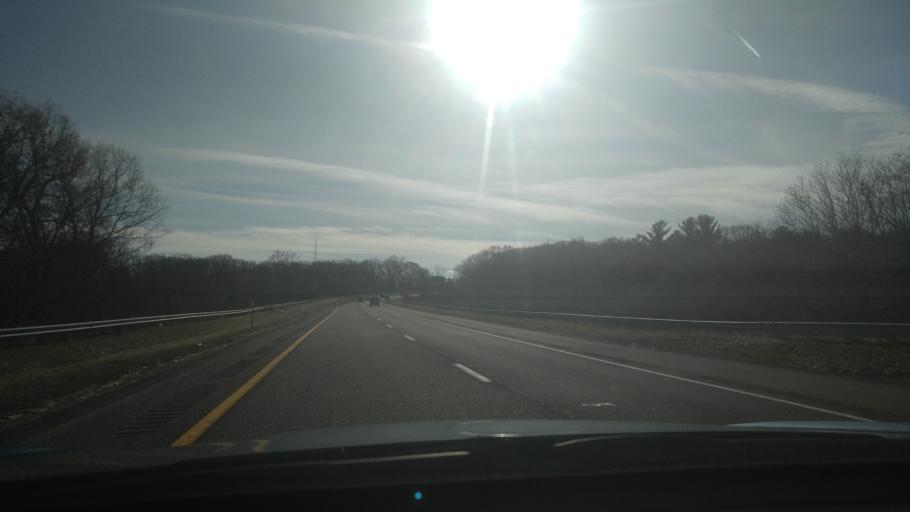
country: US
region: Rhode Island
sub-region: Providence County
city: Cumberland Hill
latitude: 41.9557
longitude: -71.4832
